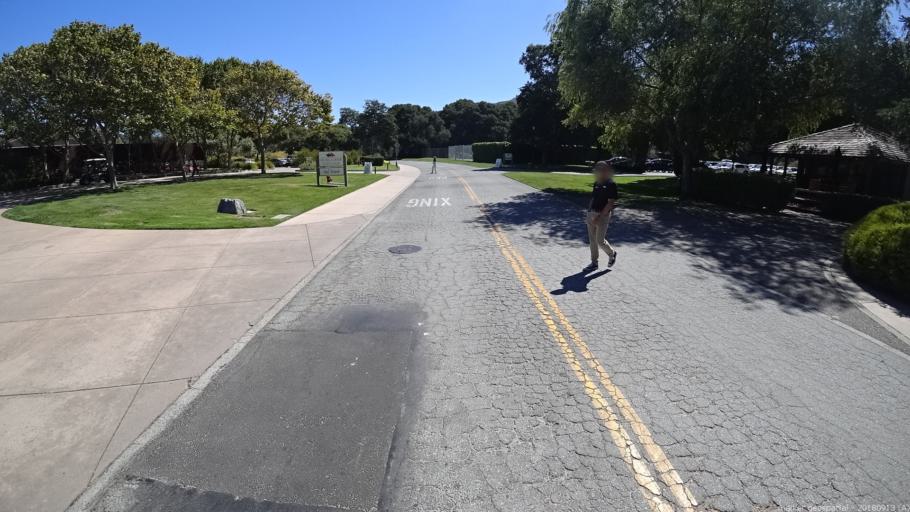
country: US
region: California
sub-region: Monterey County
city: Del Rey Oaks
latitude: 36.5305
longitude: -121.8597
